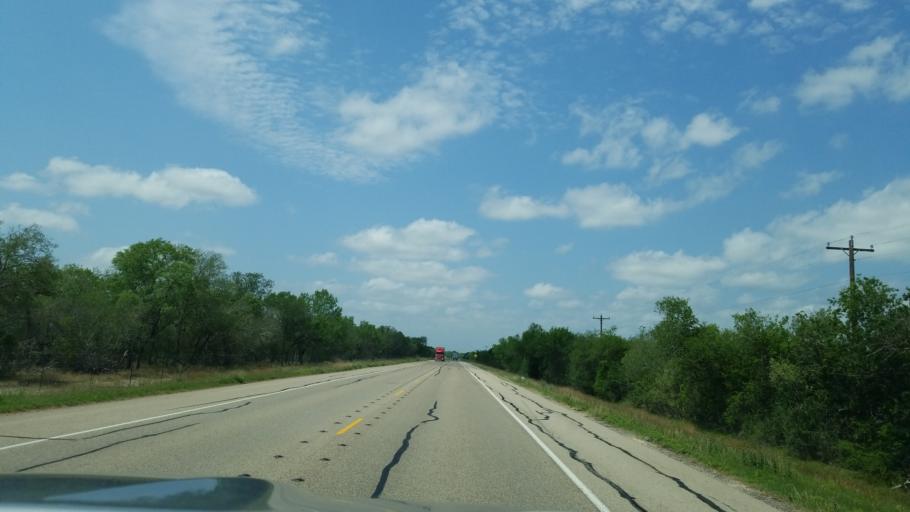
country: US
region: Texas
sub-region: Frio County
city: Pearsall
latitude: 28.9962
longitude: -99.2232
